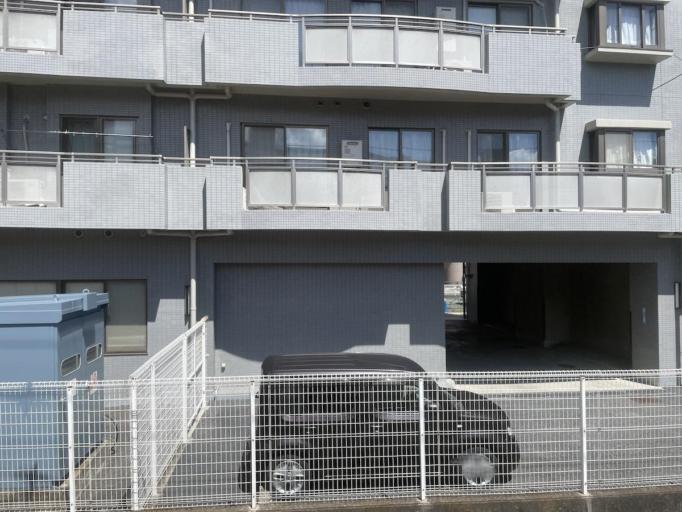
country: JP
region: Tokyo
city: Urayasu
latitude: 35.7054
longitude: 139.8324
